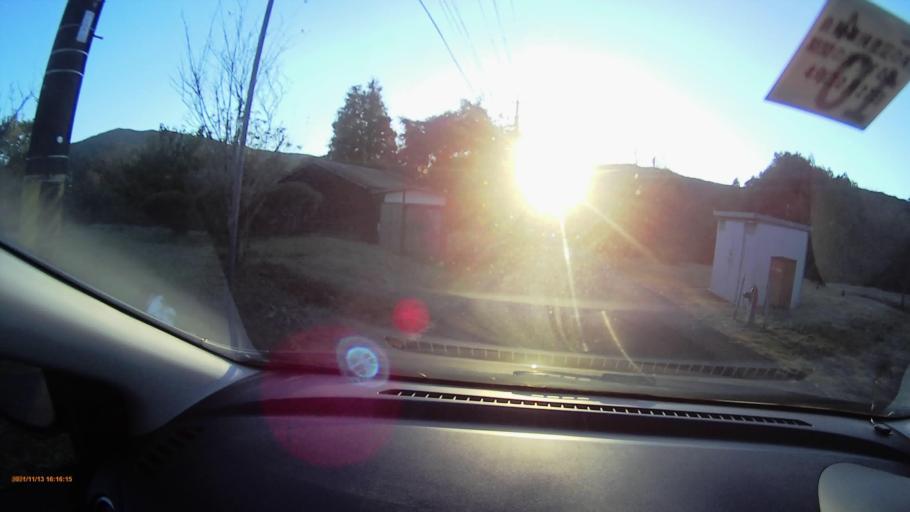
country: JP
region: Gifu
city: Nakatsugawa
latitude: 35.5771
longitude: 137.5092
